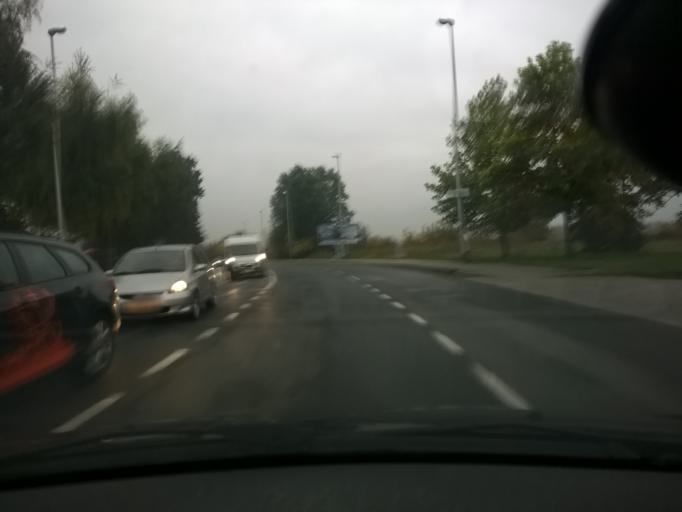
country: HR
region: Grad Zagreb
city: Jankomir
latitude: 45.7953
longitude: 15.8919
